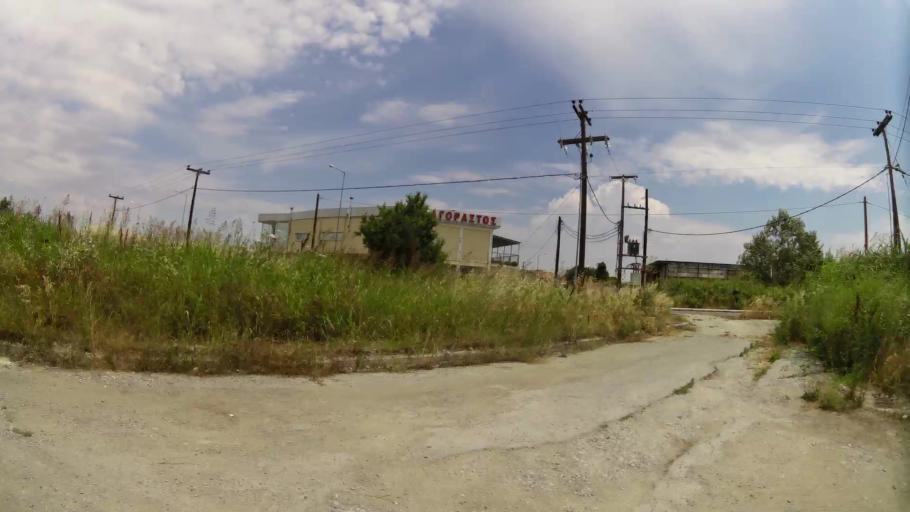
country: GR
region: Central Macedonia
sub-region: Nomos Pierias
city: Peristasi
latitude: 40.2649
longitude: 22.5253
